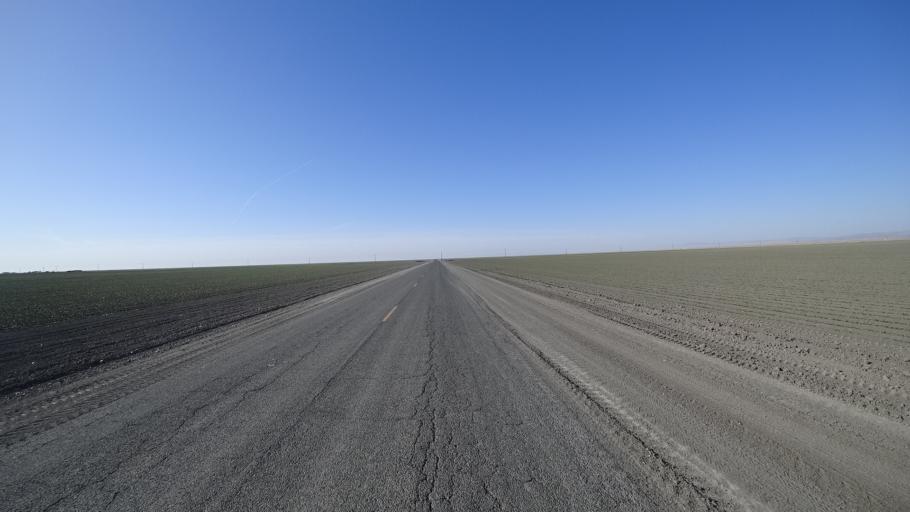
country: US
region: California
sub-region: Kings County
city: Stratford
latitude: 36.0840
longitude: -119.7979
